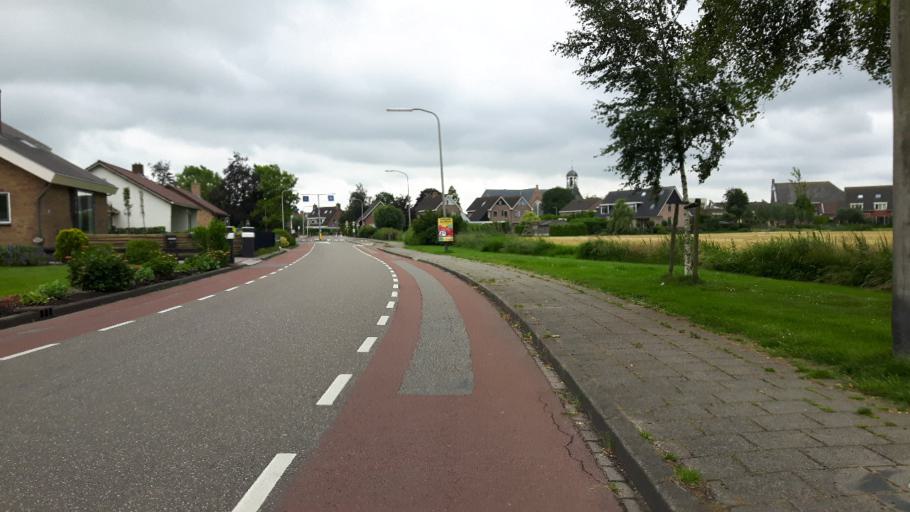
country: NL
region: Utrecht
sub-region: Gemeente Oudewater
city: Oudewater
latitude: 52.0630
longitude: 4.8208
